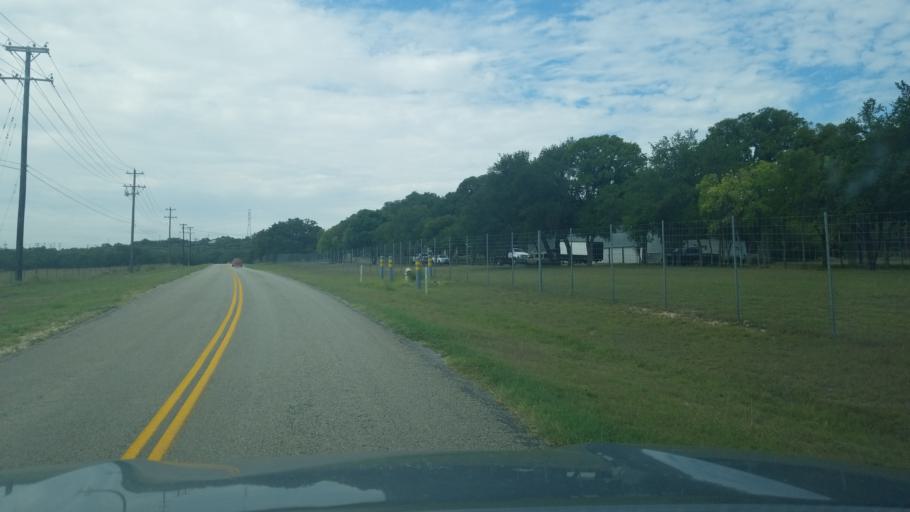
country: US
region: Texas
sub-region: Comal County
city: Bulverde
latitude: 29.7856
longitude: -98.4132
